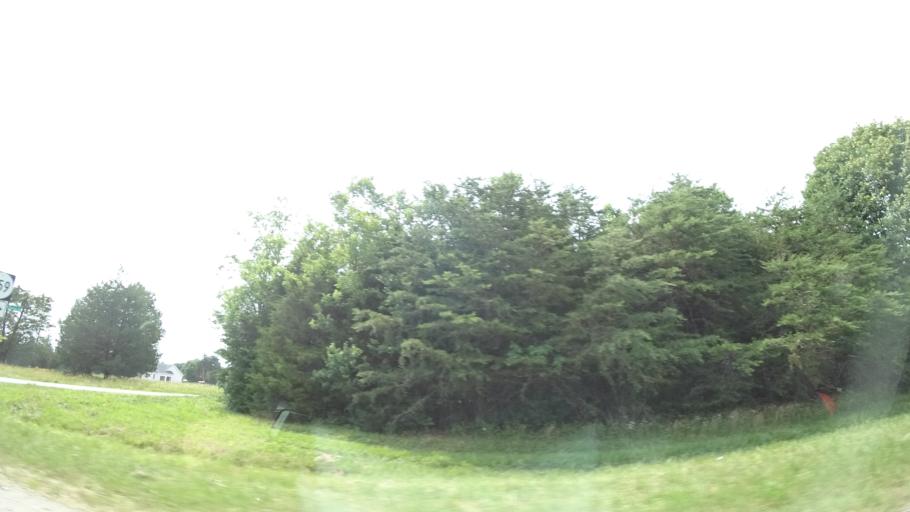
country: US
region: Virginia
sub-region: Spotsylvania County
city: Spotsylvania Courthouse
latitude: 38.1315
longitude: -77.7333
